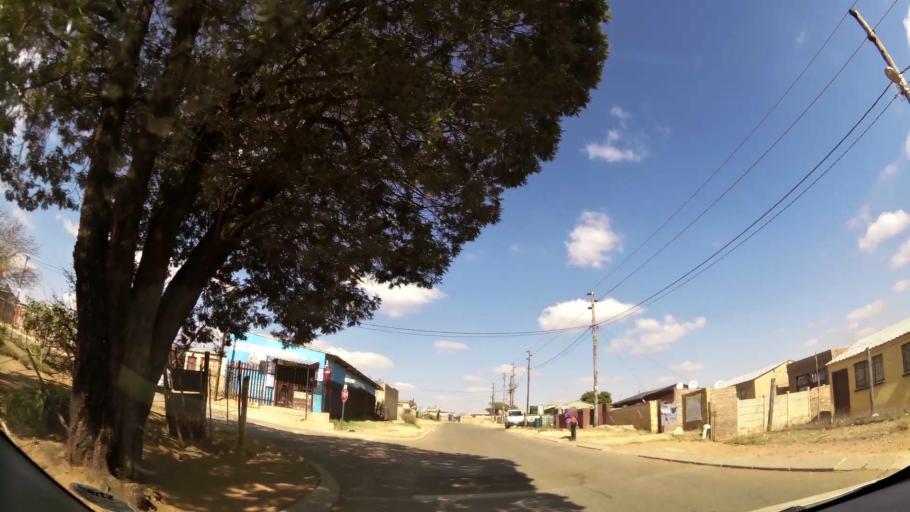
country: ZA
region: Gauteng
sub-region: West Rand District Municipality
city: Krugersdorp
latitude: -26.1433
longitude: 27.7872
